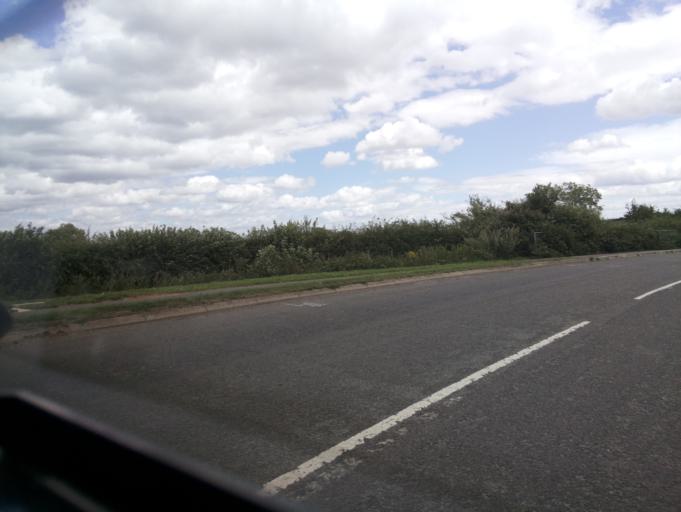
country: GB
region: England
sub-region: Nottinghamshire
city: West Bridgford
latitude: 52.9254
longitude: -1.0968
